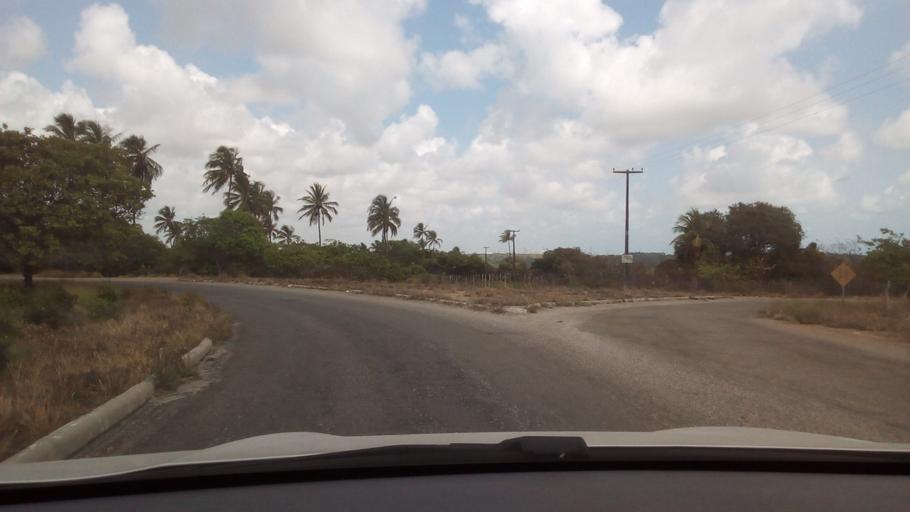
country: BR
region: Paraiba
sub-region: Conde
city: Conde
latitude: -7.2530
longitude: -34.8110
